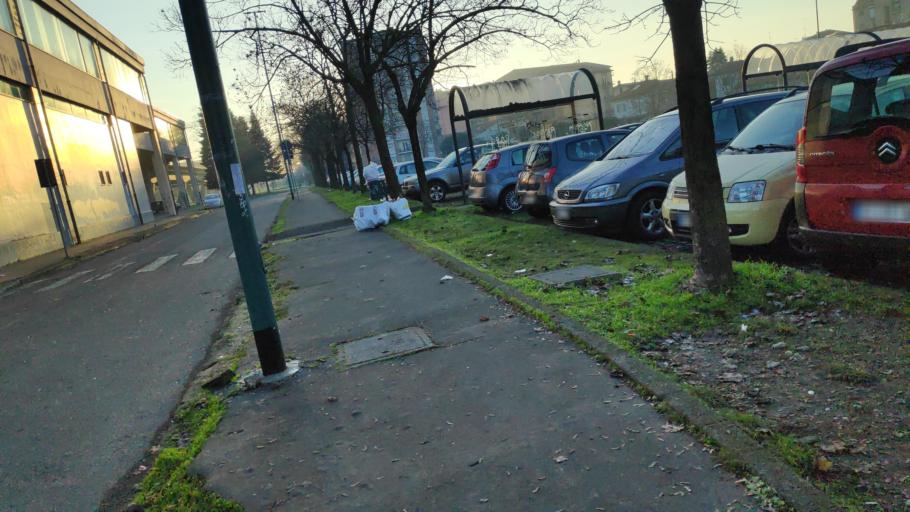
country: IT
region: Lombardy
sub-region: Citta metropolitana di Milano
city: Cologno Monzese
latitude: 45.5278
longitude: 9.2830
